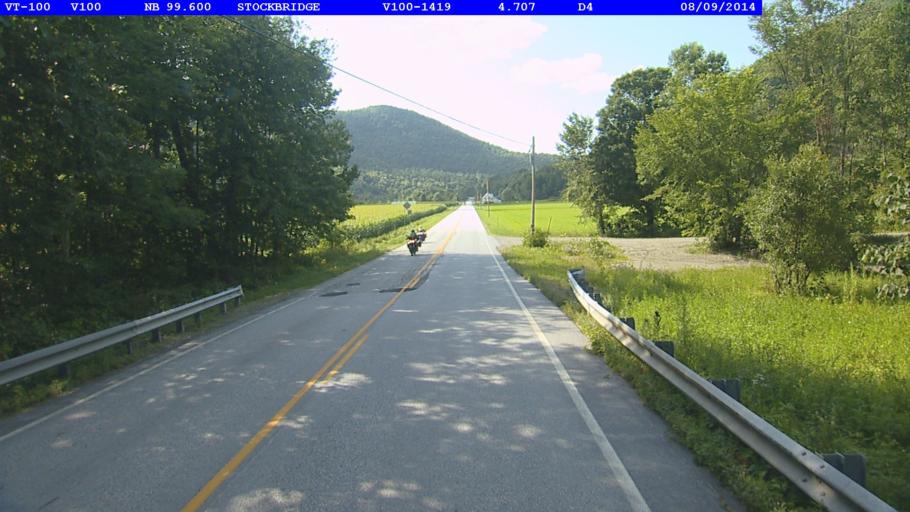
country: US
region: Vermont
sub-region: Orange County
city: Randolph
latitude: 43.8021
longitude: -72.7759
